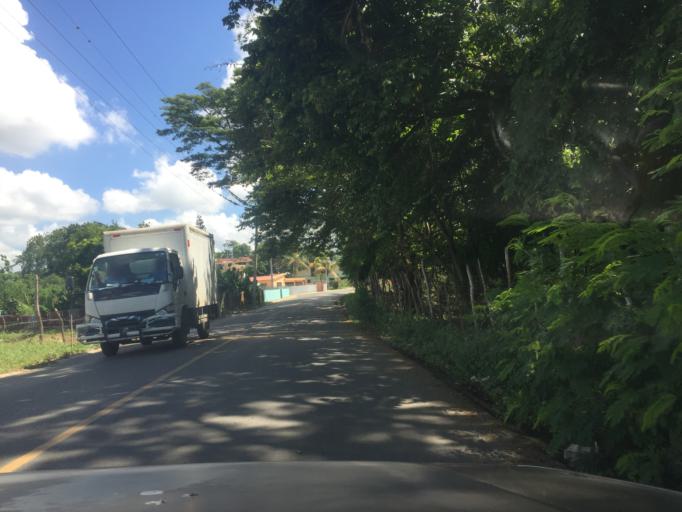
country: DO
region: Santiago
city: Santiago de los Caballeros
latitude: 19.4454
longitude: -70.7566
